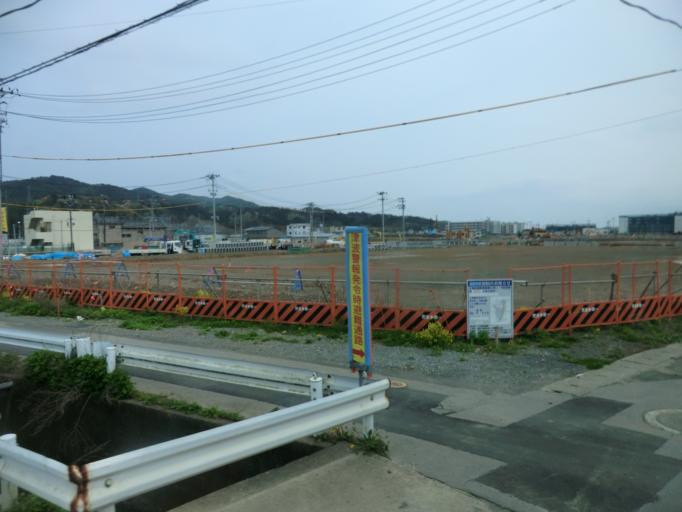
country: JP
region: Iwate
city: Ofunato
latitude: 38.9200
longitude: 141.5824
